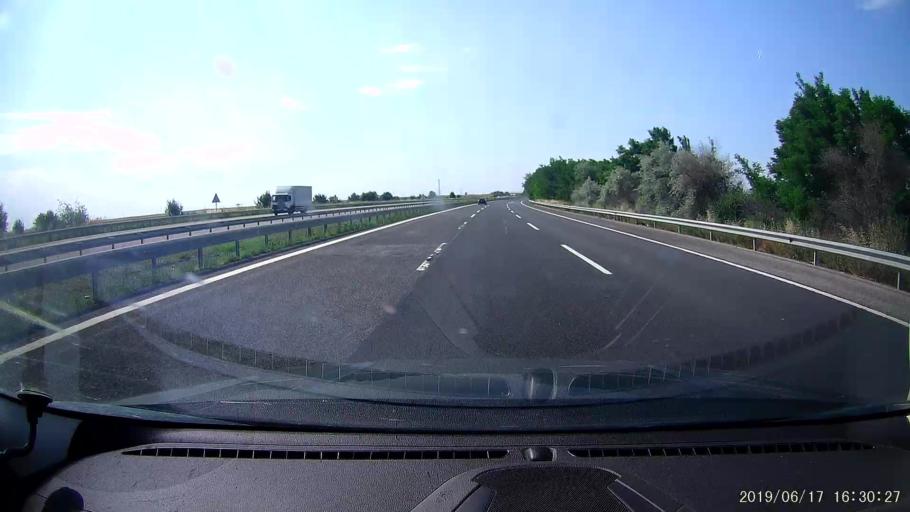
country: TR
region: Tekirdag
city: Beyazkoy
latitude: 41.3467
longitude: 27.6533
